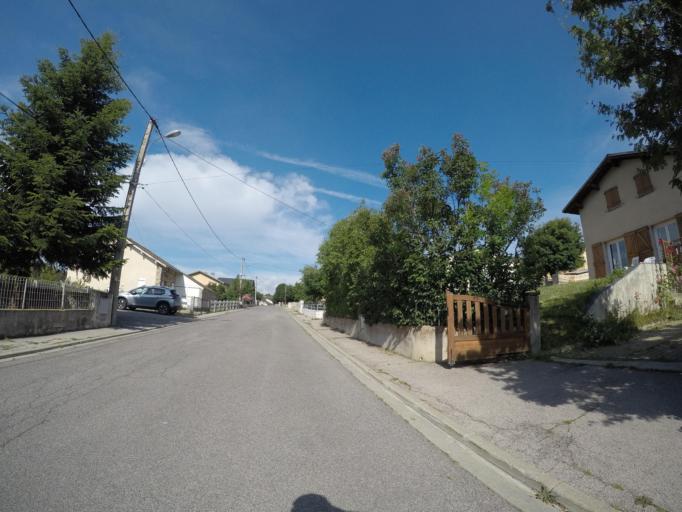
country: ES
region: Catalonia
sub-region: Provincia de Girona
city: Llivia
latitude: 42.5013
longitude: 2.1113
